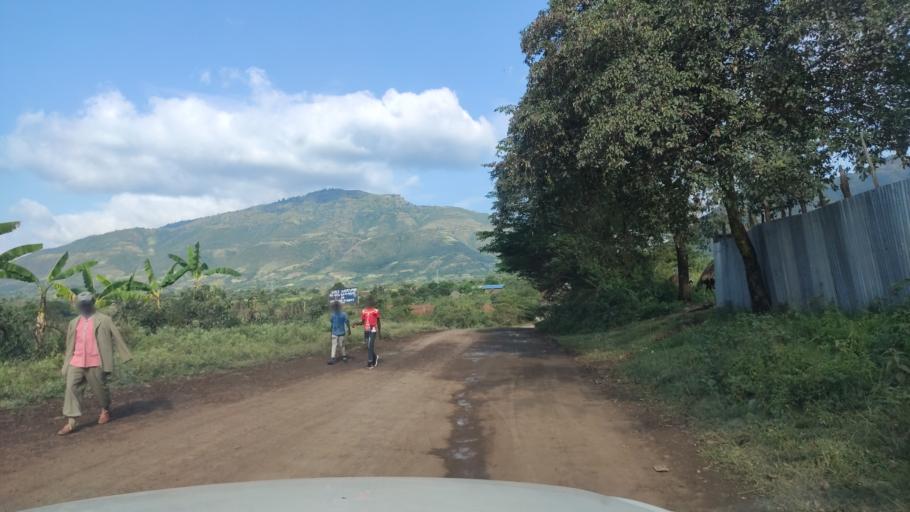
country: ET
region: Southern Nations, Nationalities, and People's Region
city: Felege Neway
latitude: 6.4263
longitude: 37.3181
